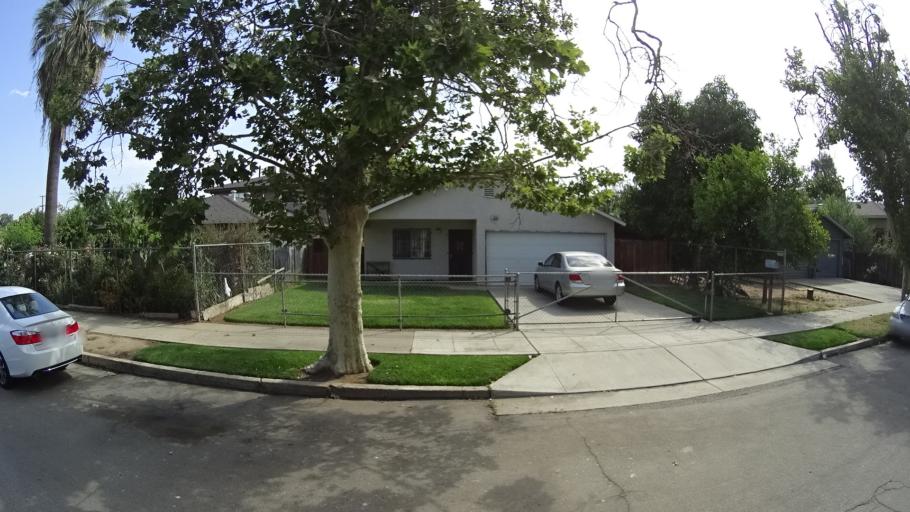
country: US
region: California
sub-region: Fresno County
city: Fresno
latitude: 36.7340
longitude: -119.8043
